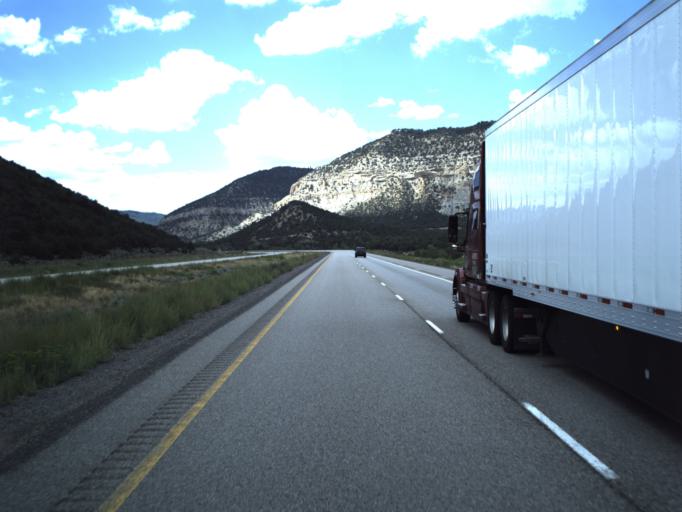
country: US
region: Utah
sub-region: Wayne County
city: Loa
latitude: 38.7568
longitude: -111.4019
